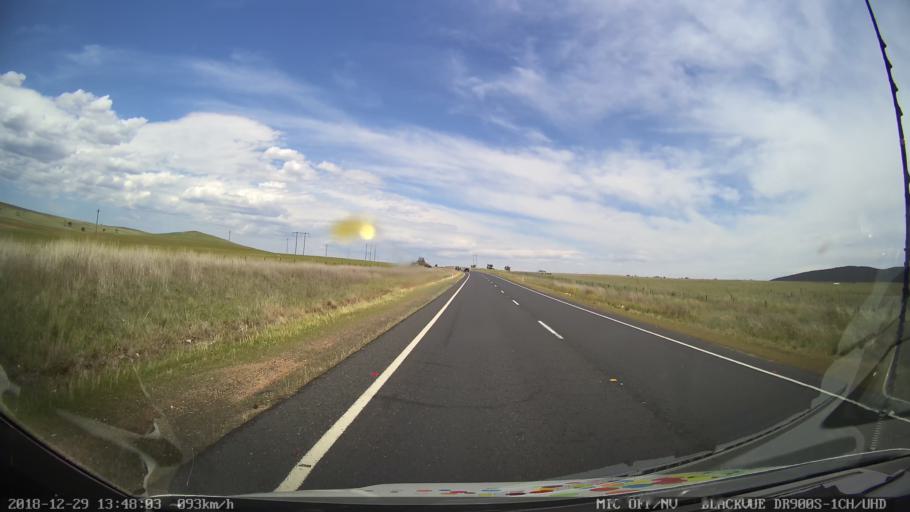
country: AU
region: New South Wales
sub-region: Cooma-Monaro
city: Cooma
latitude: -36.1352
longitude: 149.1458
